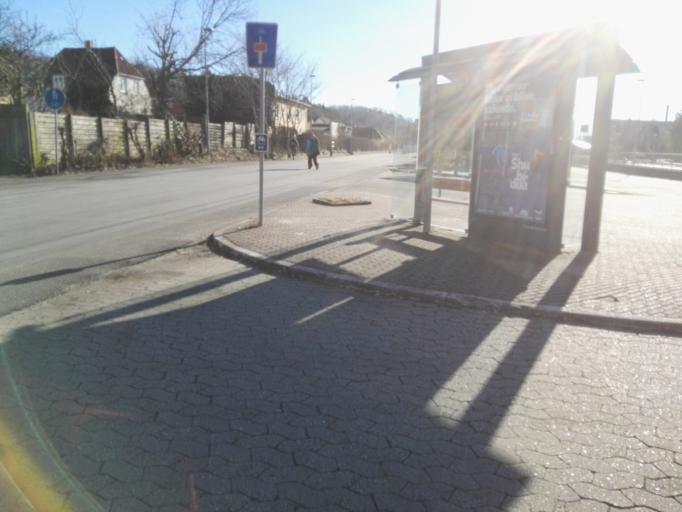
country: DK
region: Capital Region
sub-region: Halsnaes Kommune
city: Frederiksvaerk
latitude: 55.9684
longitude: 12.0197
